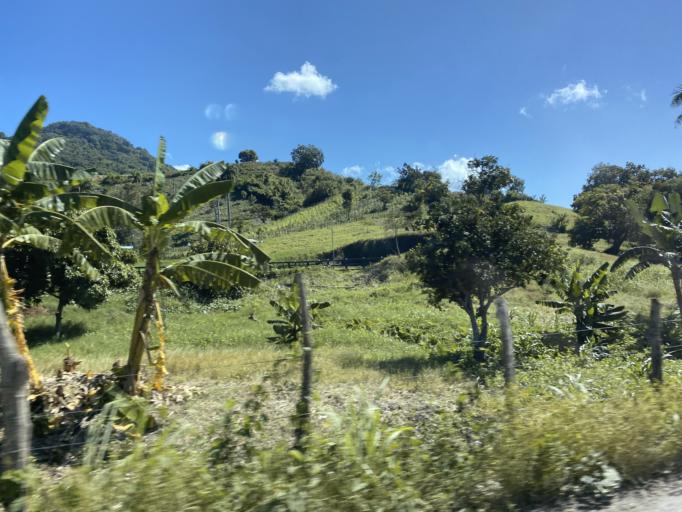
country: DO
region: Puerto Plata
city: Imbert
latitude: 19.8171
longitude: -70.7793
